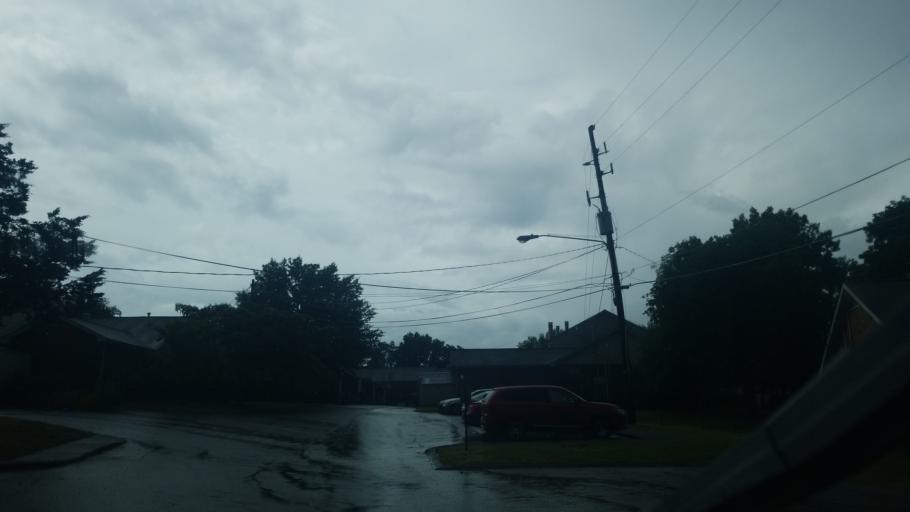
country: US
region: Tennessee
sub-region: Rutherford County
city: La Vergne
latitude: 36.1056
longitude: -86.6006
